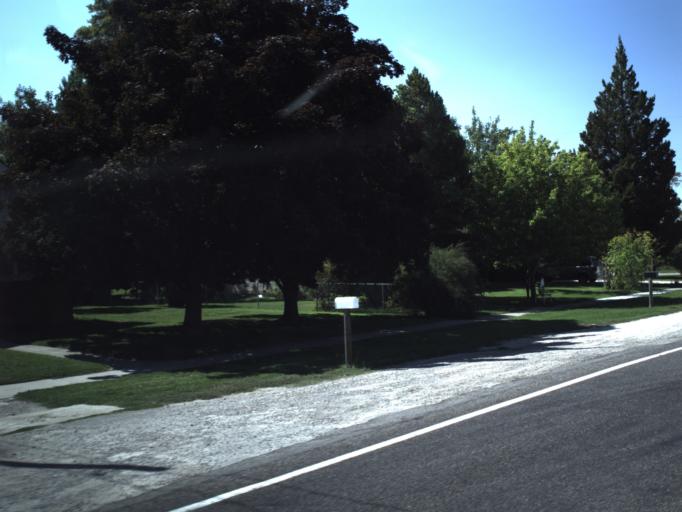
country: US
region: Utah
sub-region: Cache County
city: Smithfield
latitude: 41.8387
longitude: -111.8416
